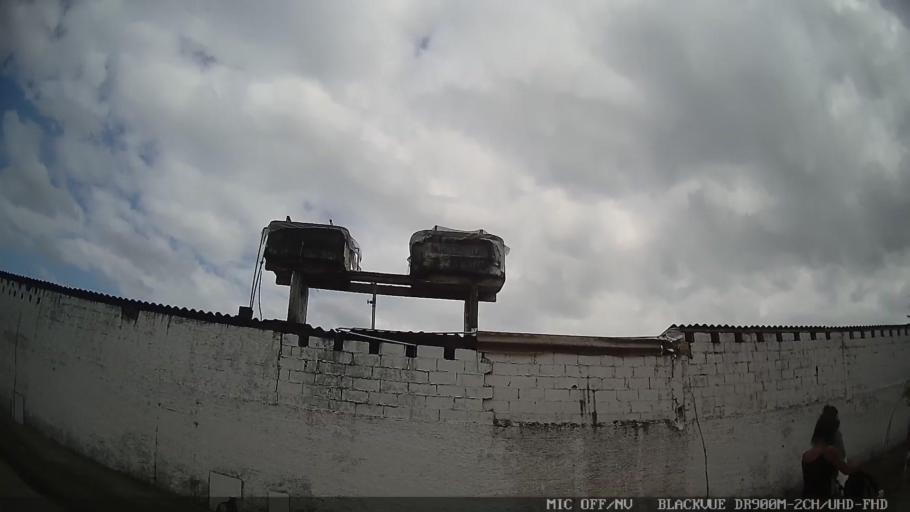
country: BR
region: Sao Paulo
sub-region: Guaruja
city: Guaruja
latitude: -23.9882
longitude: -46.2755
